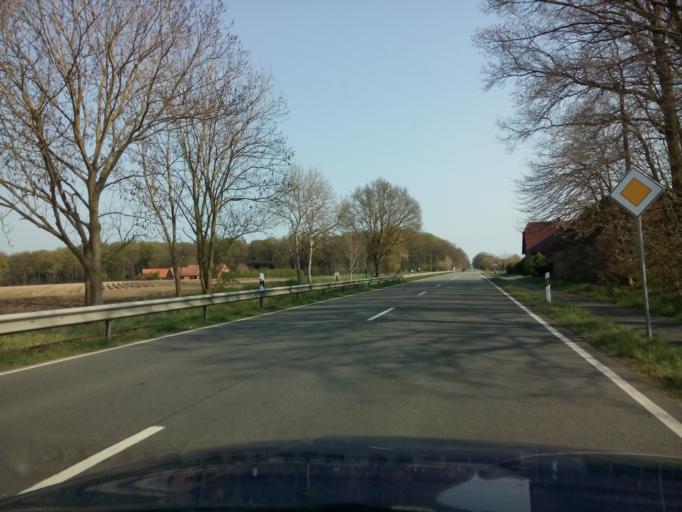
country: DE
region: Lower Saxony
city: Bruchhausen-Vilsen
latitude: 52.7998
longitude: 8.9765
